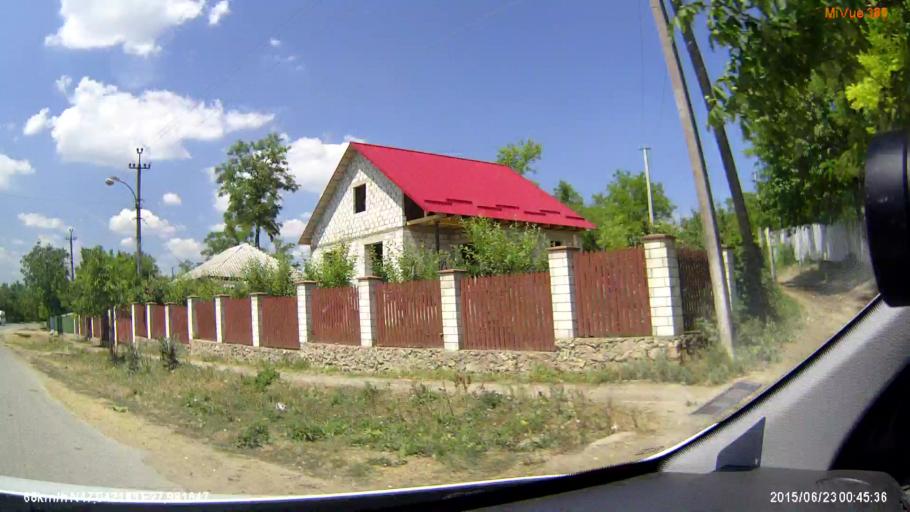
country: RO
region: Iasi
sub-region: Comuna Grozesti
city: Grozesti
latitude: 47.0421
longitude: 27.9819
